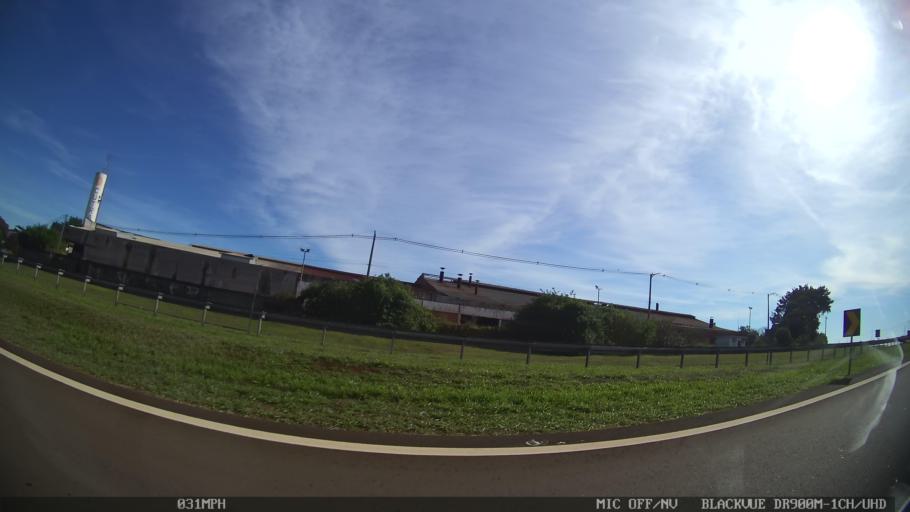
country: BR
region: Sao Paulo
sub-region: Cordeiropolis
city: Cordeiropolis
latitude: -22.4998
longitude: -47.3999
